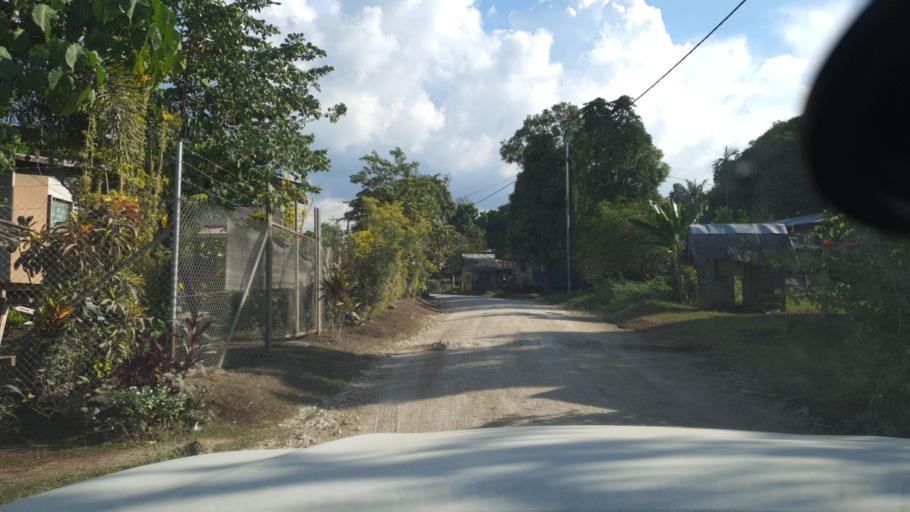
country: SB
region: Guadalcanal
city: Honiara
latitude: -9.4502
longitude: 159.9941
